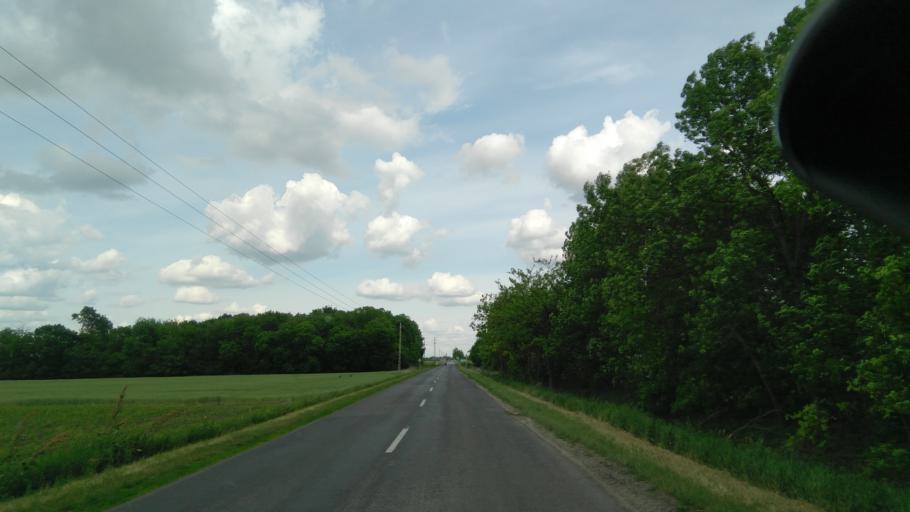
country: HU
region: Bekes
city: Battonya
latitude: 46.2934
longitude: 20.9823
